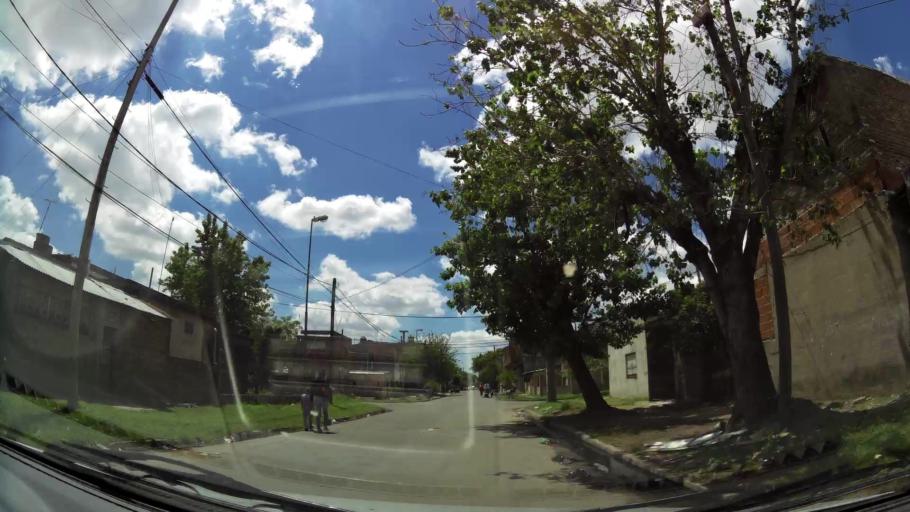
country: AR
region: Buenos Aires
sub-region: Partido de Lanus
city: Lanus
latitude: -34.6963
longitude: -58.4348
